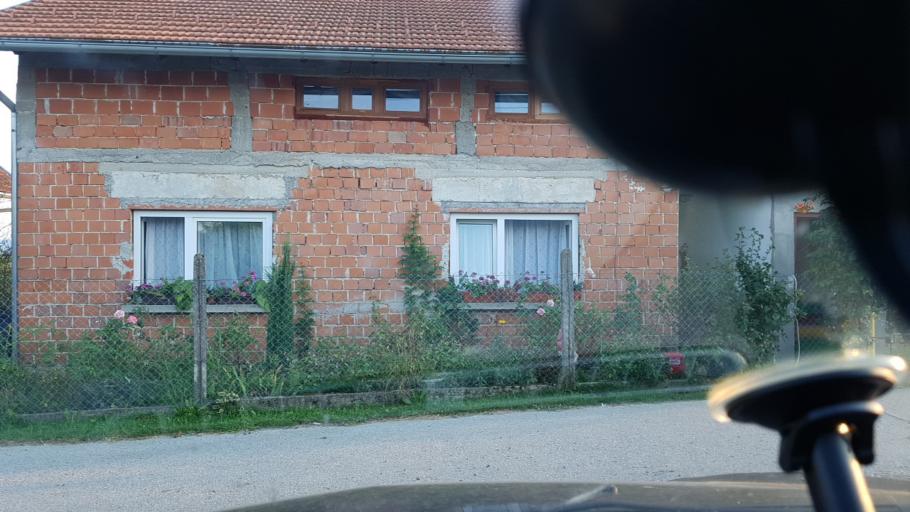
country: HR
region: Krapinsko-Zagorska
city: Selnica
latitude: 46.0606
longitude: 16.0396
